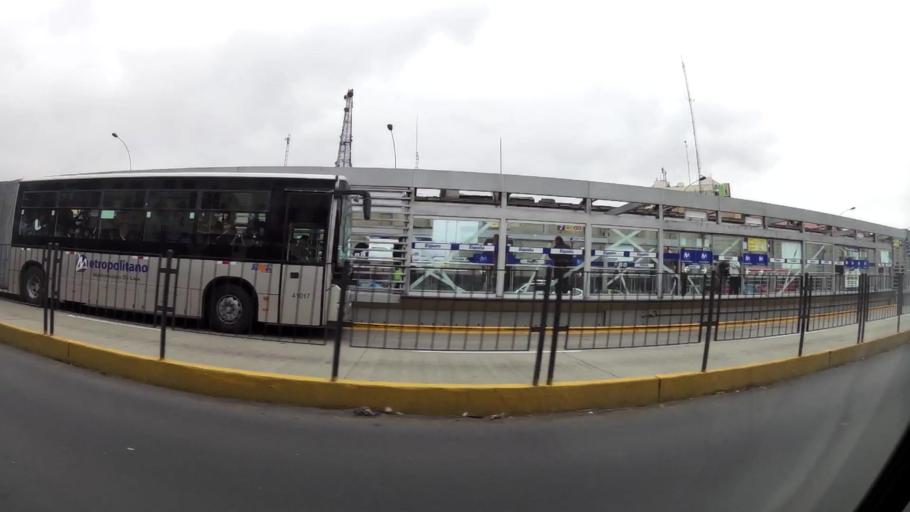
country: PE
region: Lima
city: Lima
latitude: -12.0572
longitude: -77.0422
